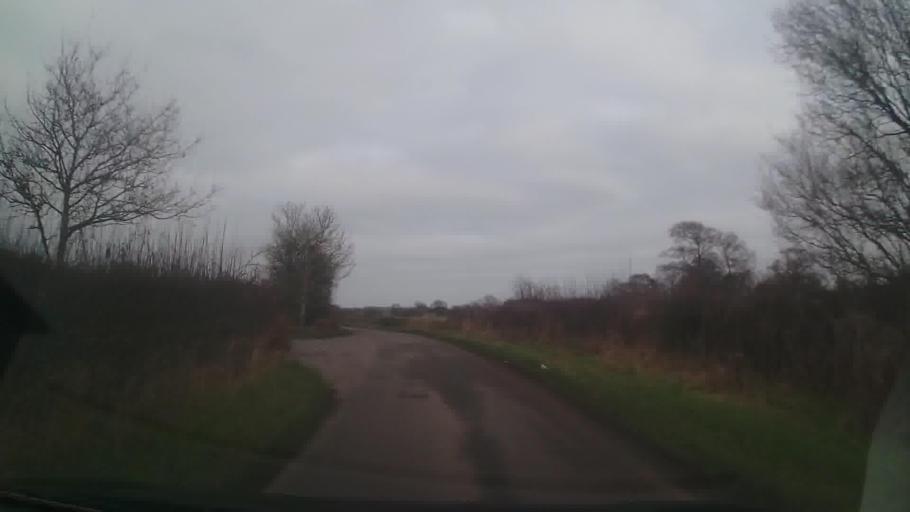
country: GB
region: England
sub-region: Shropshire
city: Petton
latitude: 52.8346
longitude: -2.7877
